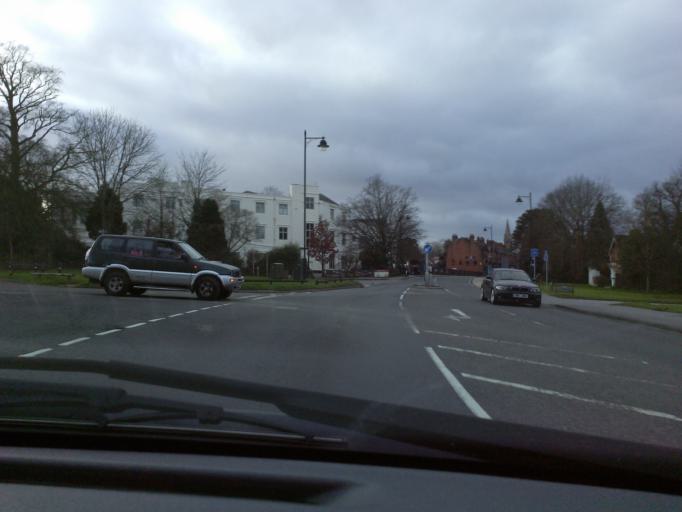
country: GB
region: England
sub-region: Hampshire
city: Lyndhurst
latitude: 50.8725
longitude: -1.5705
